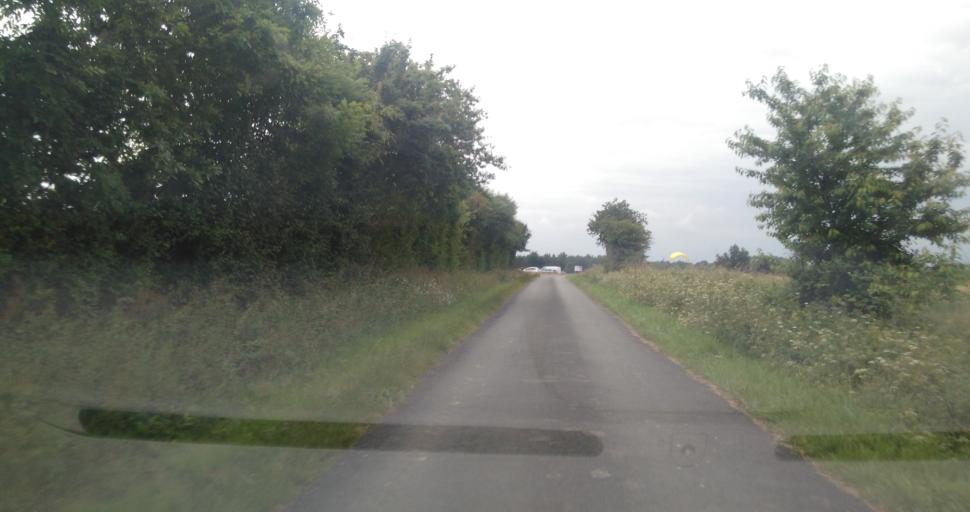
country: FR
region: Pays de la Loire
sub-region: Departement de la Vendee
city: Saint-Georges-de-Montaigu
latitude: 46.9304
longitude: -1.3223
